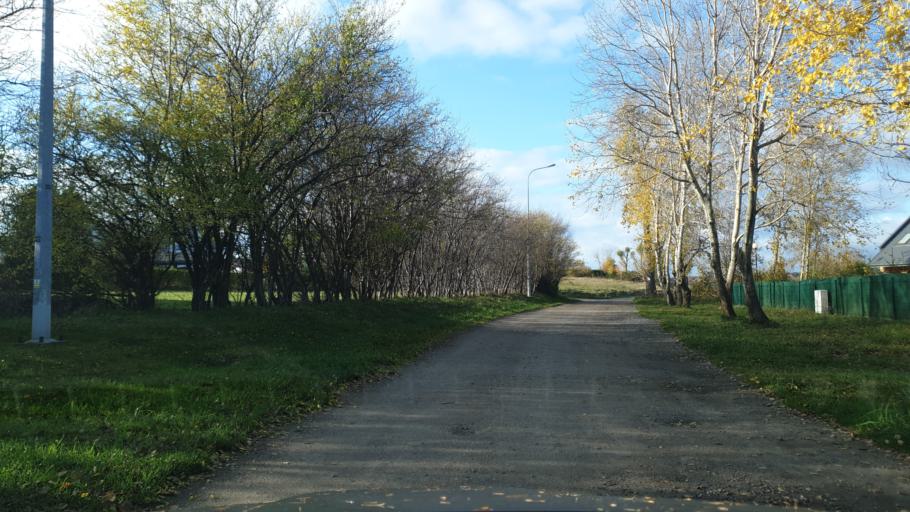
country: PL
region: Pomeranian Voivodeship
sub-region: Powiat pucki
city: Jastrzebia Gora
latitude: 54.8244
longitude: 18.2395
